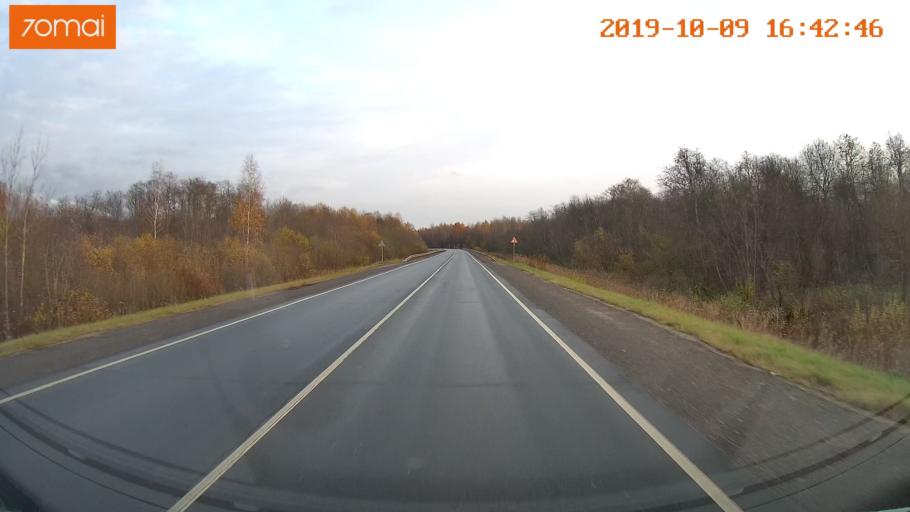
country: RU
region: Kostroma
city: Volgorechensk
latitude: 57.4587
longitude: 41.1071
